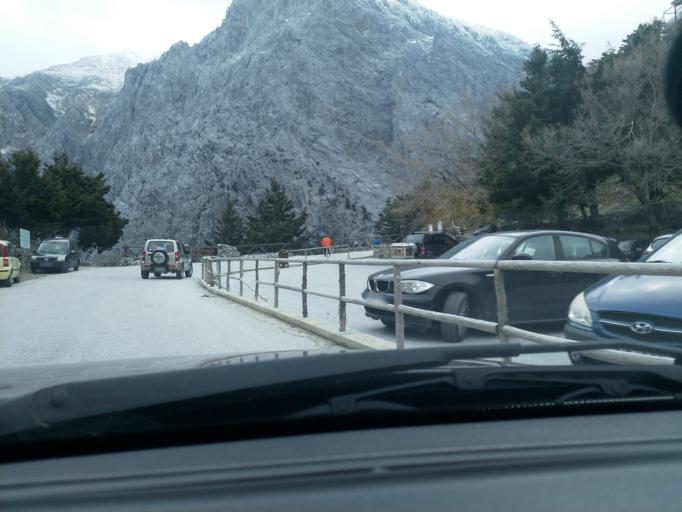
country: GR
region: Crete
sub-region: Nomos Chanias
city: Perivolia
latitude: 35.3083
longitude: 23.9183
